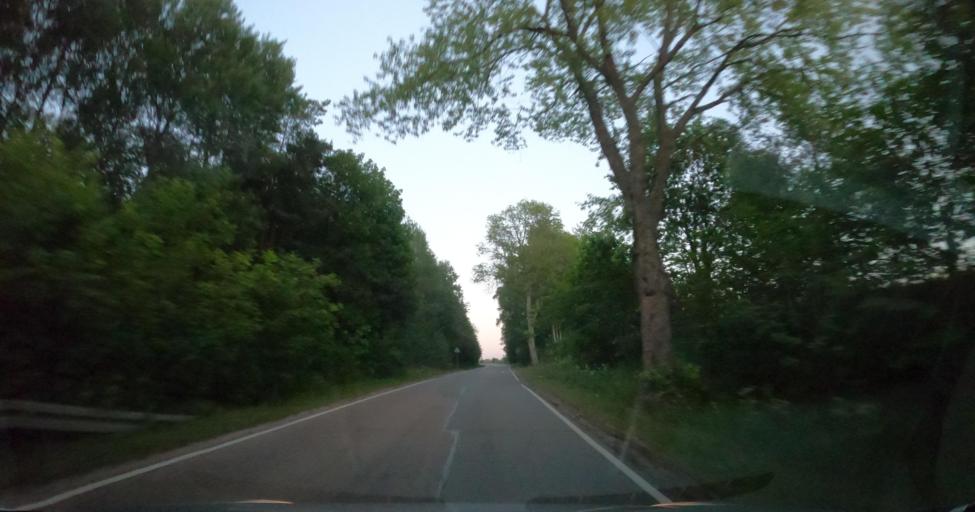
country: PL
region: Pomeranian Voivodeship
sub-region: Powiat wejherowski
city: Szemud
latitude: 54.4643
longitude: 18.1267
